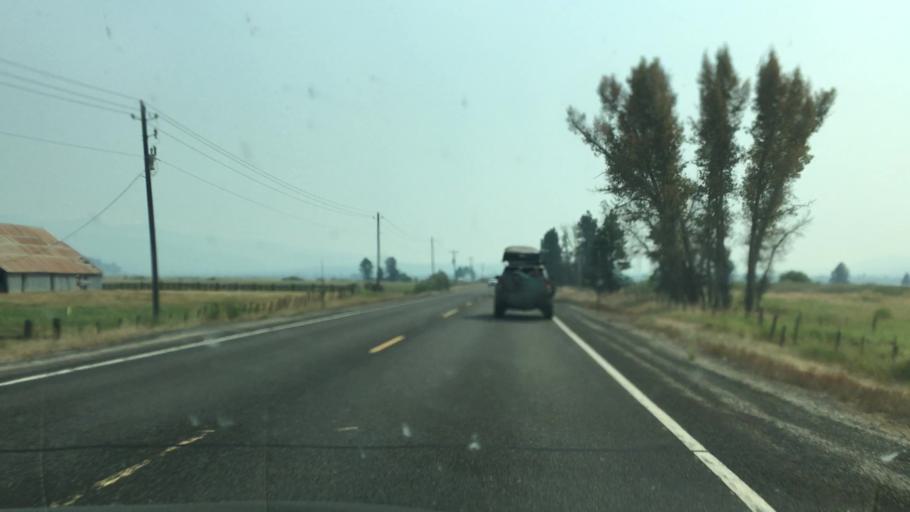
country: US
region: Idaho
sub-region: Valley County
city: Cascade
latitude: 44.4328
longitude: -115.9994
